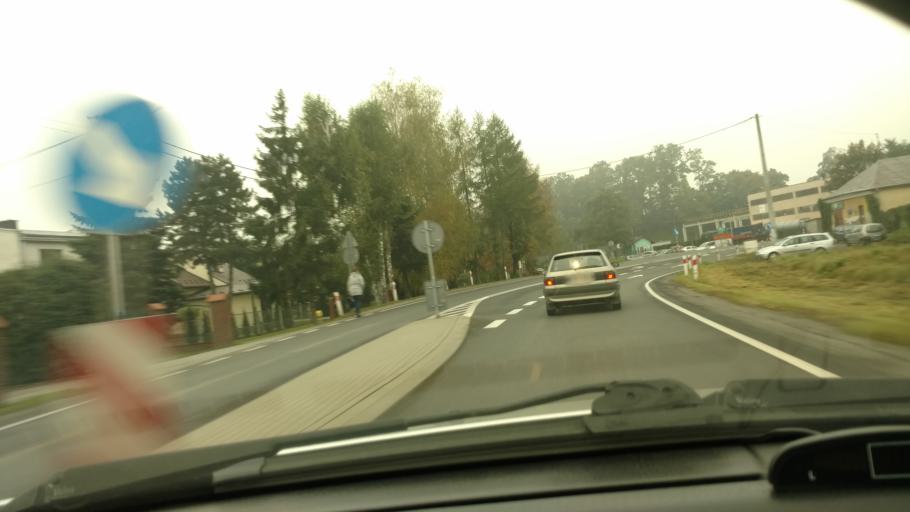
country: PL
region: Lesser Poland Voivodeship
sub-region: Powiat gorlicki
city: Kobylanka
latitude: 49.7048
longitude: 21.2372
